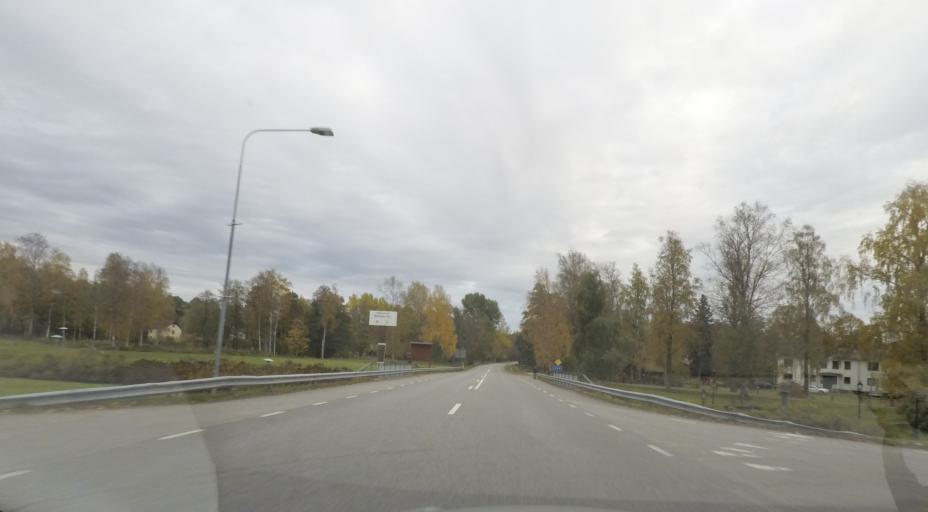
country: SE
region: OErebro
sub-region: Hallefors Kommun
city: Haellefors
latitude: 59.7059
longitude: 14.5444
